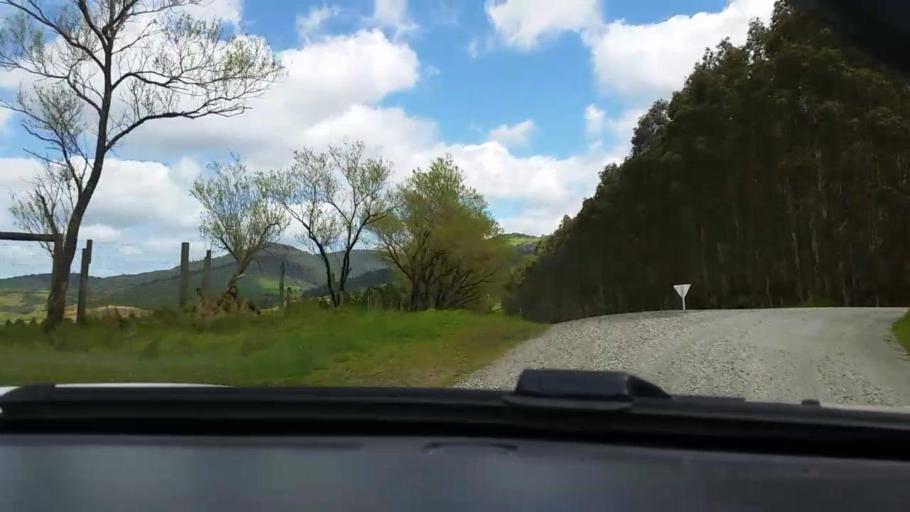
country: NZ
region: Otago
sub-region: Clutha District
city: Papatowai
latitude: -46.5860
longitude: 169.1564
